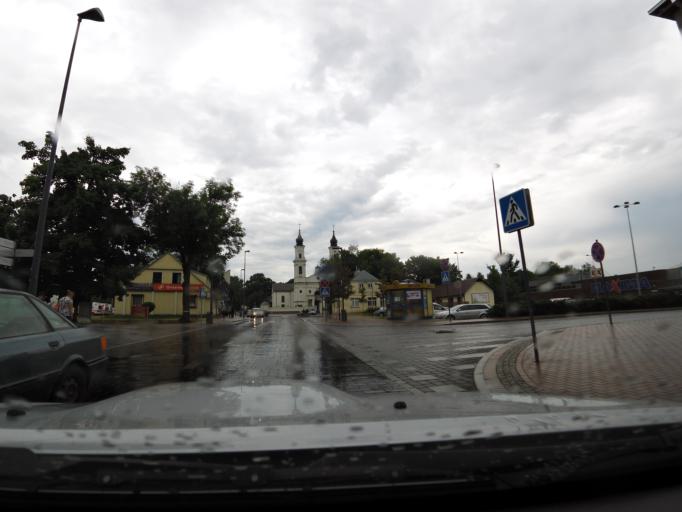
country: LT
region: Marijampoles apskritis
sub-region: Marijampole Municipality
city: Marijampole
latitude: 54.5552
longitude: 23.3472
